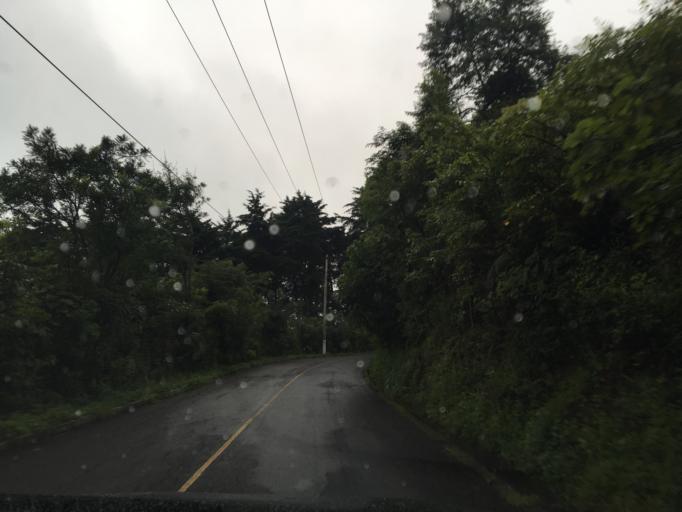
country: GT
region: Guatemala
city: Santa Catarina Pinula
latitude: 14.5474
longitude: -90.4996
